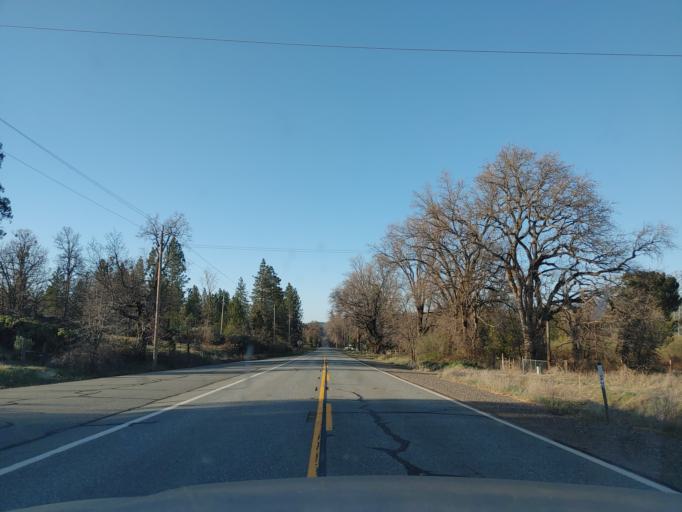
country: US
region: California
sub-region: Shasta County
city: Burney
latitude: 40.8084
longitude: -121.9399
